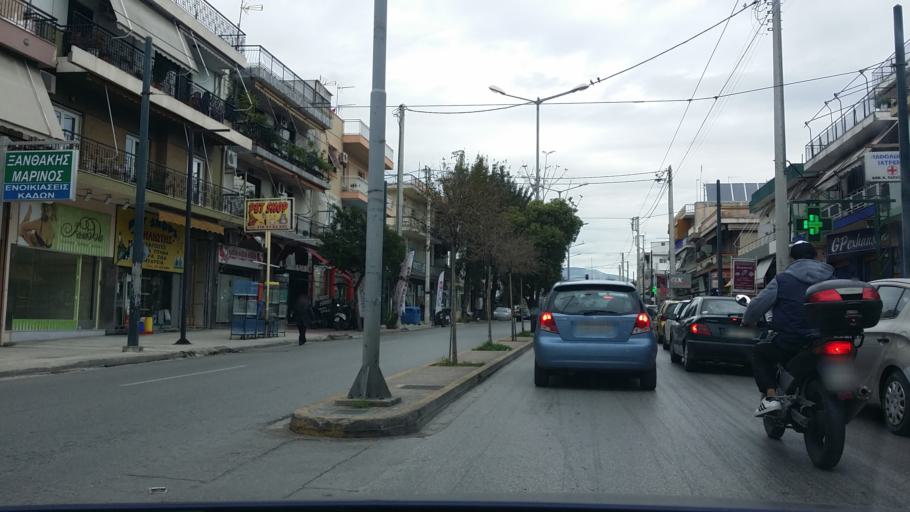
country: GR
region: Attica
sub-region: Nomarchia Athinas
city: Peristeri
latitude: 38.0206
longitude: 23.6937
